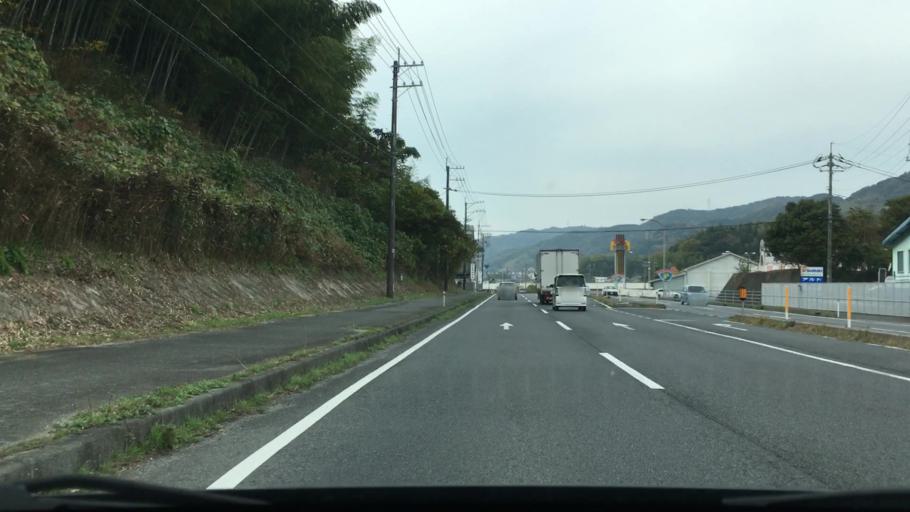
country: JP
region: Yamaguchi
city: Kudamatsu
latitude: 34.0336
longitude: 131.8956
